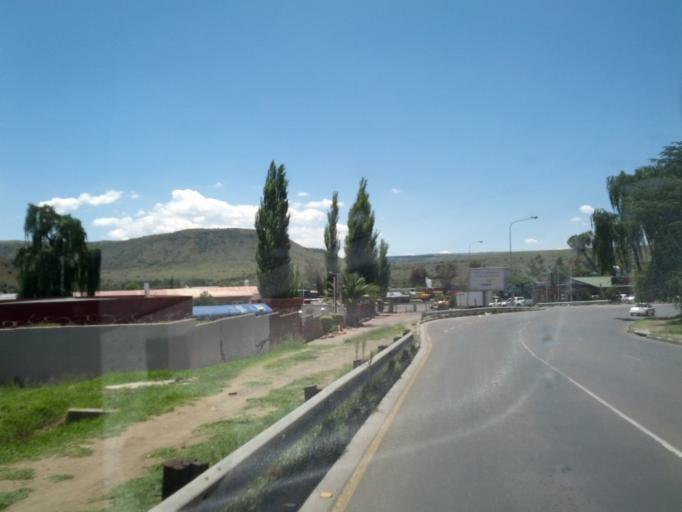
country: LS
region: Maseru
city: Maseru
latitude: -29.2999
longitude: 27.4689
